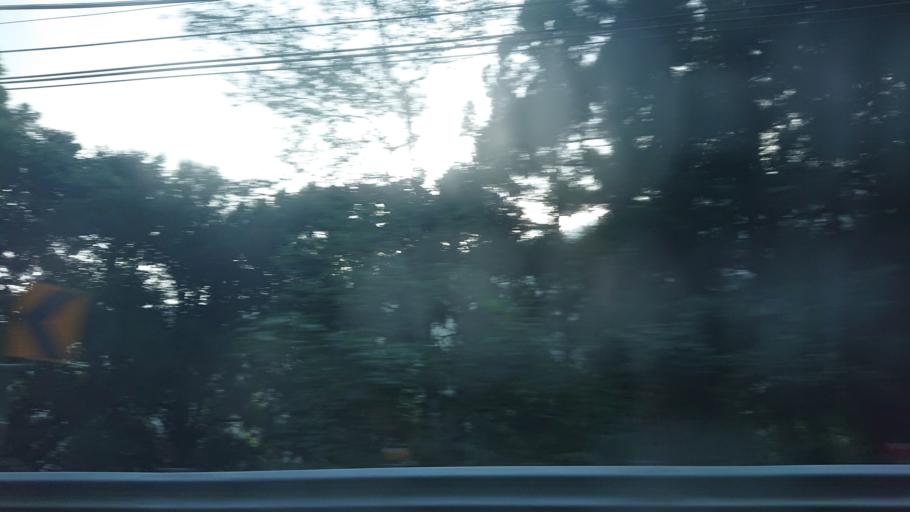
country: TW
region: Taiwan
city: Lugu
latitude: 23.4871
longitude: 120.7489
